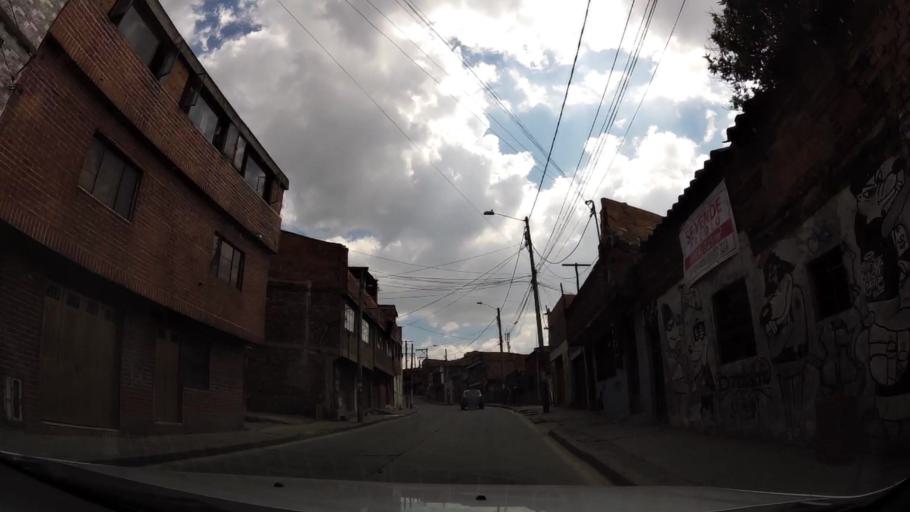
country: CO
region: Bogota D.C.
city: Bogota
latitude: 4.5640
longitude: -74.0880
